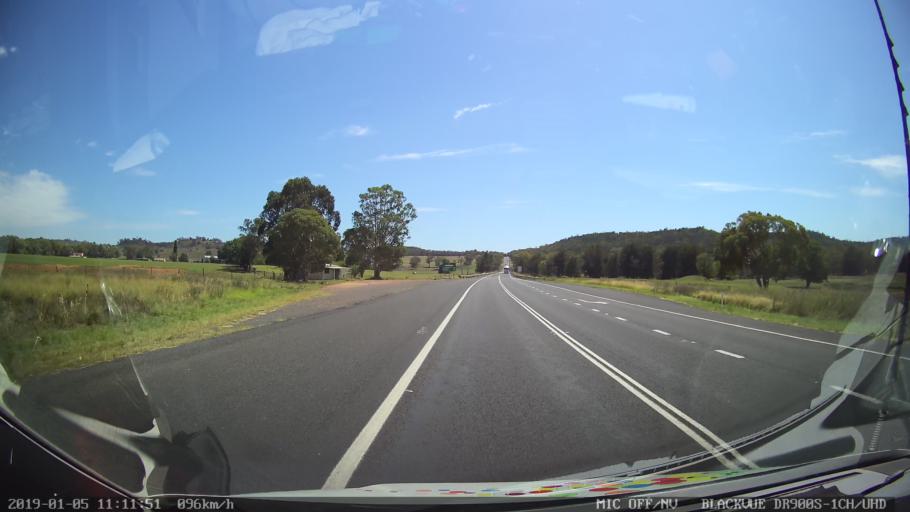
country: AU
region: New South Wales
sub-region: Warrumbungle Shire
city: Coonabarabran
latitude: -31.3882
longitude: 149.2540
